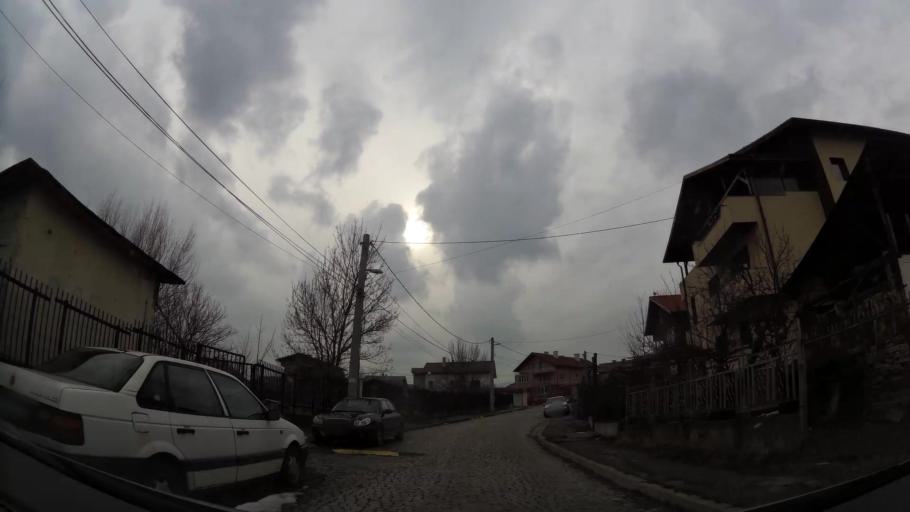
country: BG
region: Sofiya
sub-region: Obshtina Bozhurishte
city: Bozhurishte
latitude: 42.6956
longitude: 23.2243
